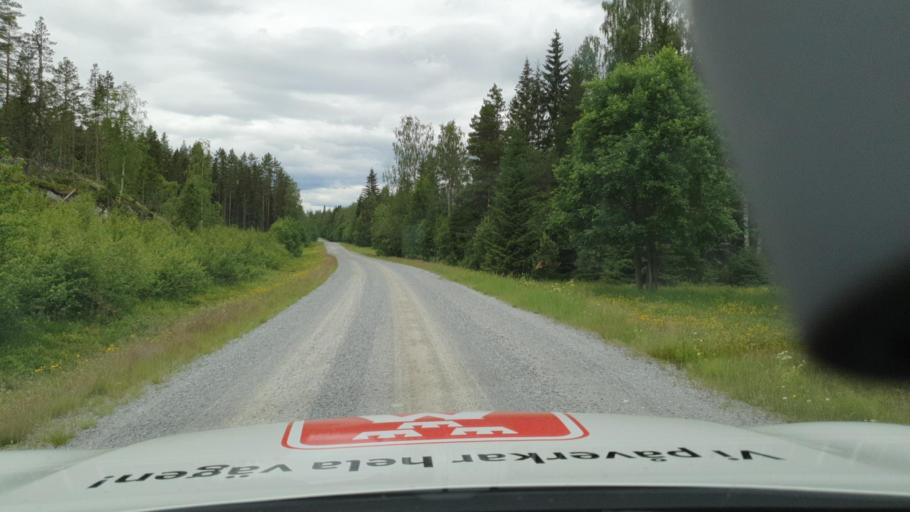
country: SE
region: Vaesterbotten
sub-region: Nordmalings Kommun
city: Nordmaling
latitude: 63.7337
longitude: 19.4216
